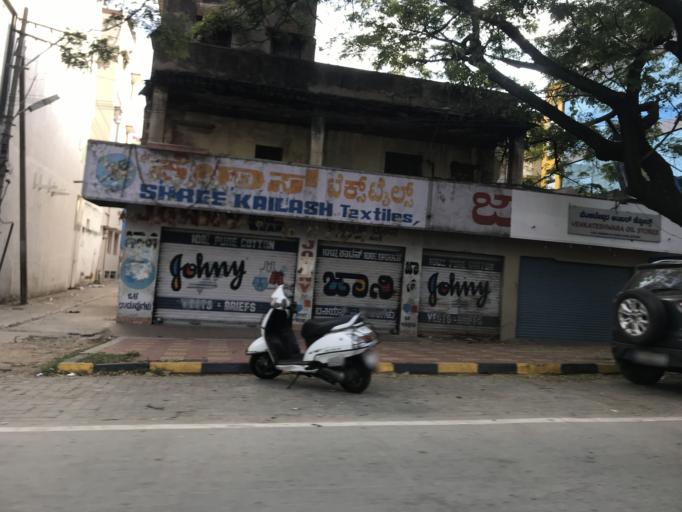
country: IN
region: Karnataka
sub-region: Mysore
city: Mysore
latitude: 12.3023
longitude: 76.6458
